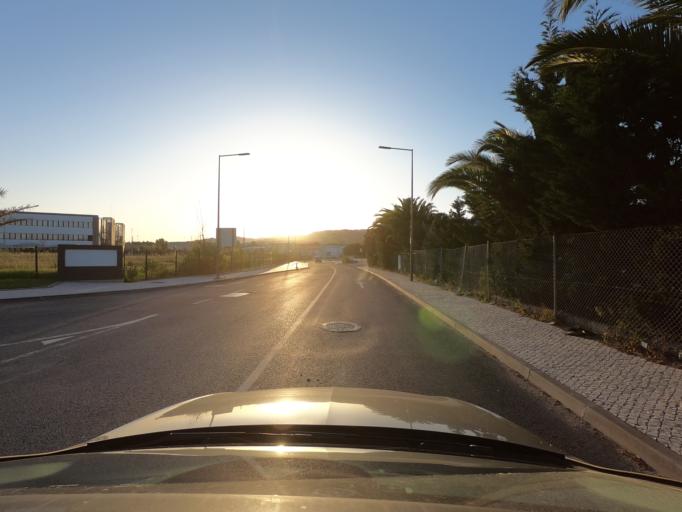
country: PT
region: Lisbon
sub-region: Cascais
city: Alcabideche
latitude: 38.7579
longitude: -9.3756
